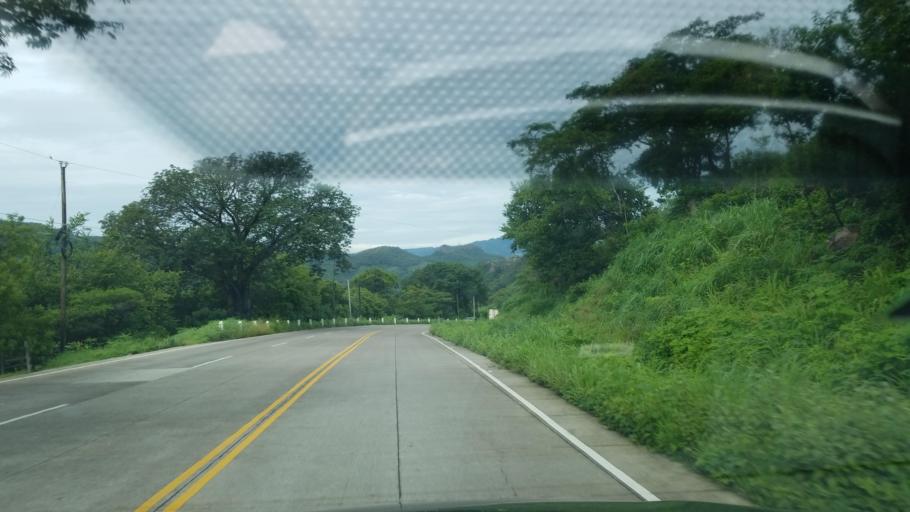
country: HN
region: Francisco Morazan
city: El Porvenir
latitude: 13.6983
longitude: -87.3227
